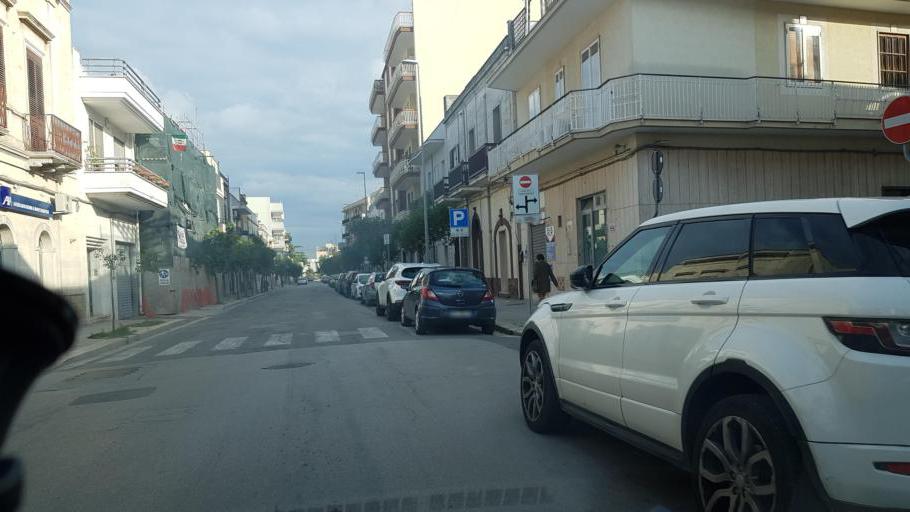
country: IT
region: Apulia
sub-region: Provincia di Brindisi
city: Francavilla Fontana
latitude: 40.5266
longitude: 17.5857
